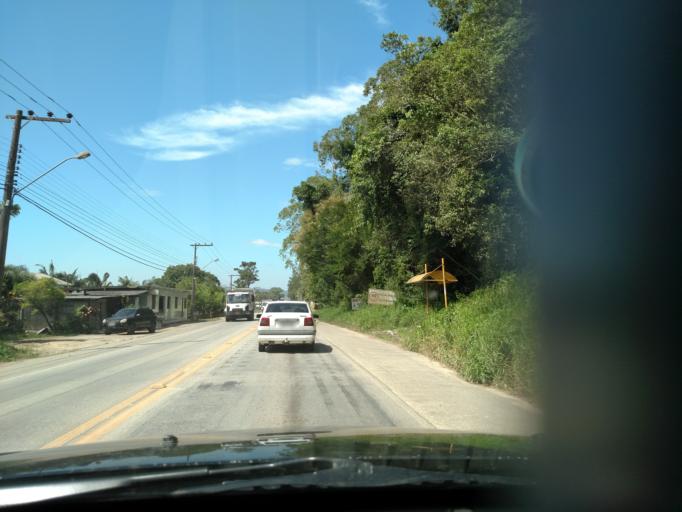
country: BR
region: Santa Catarina
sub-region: Itajai
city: Itajai
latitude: -26.8903
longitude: -48.7576
